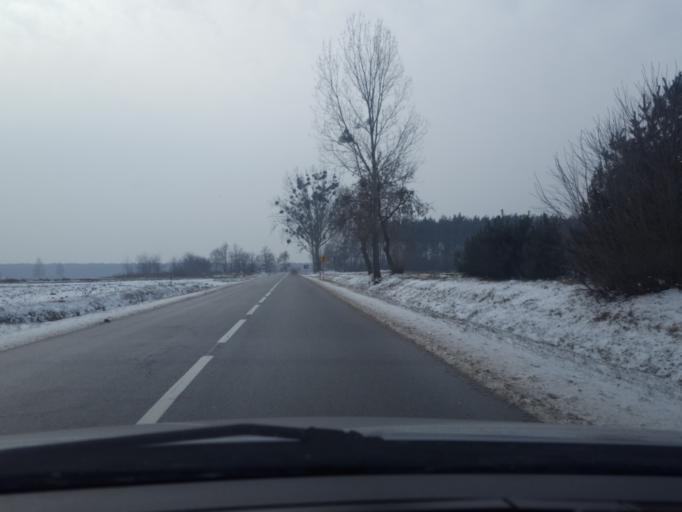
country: PL
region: Lodz Voivodeship
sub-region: Powiat brzezinski
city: Brzeziny
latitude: 51.8351
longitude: 19.8023
